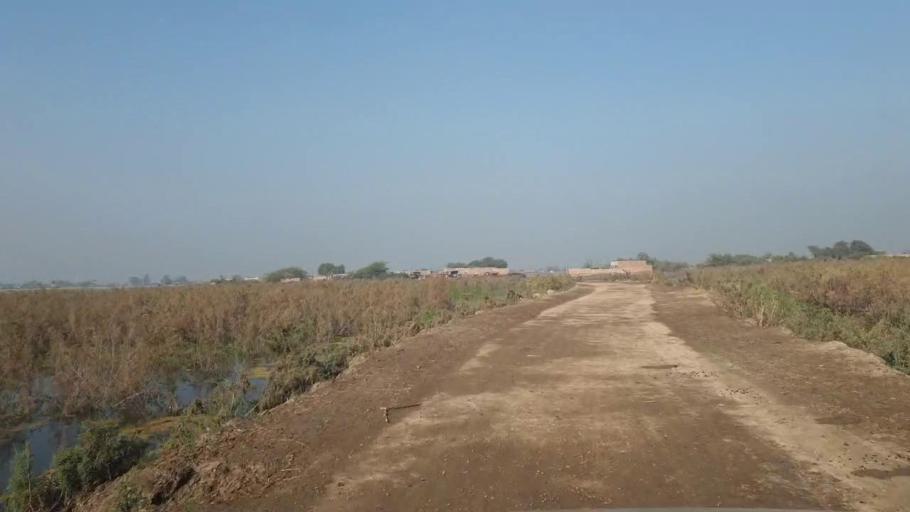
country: PK
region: Sindh
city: Shahdadpur
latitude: 25.9437
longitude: 68.5838
